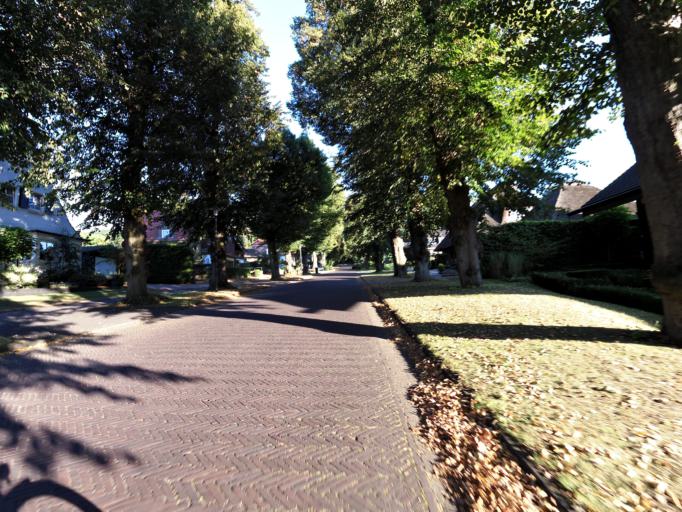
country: DE
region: North Rhine-Westphalia
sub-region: Regierungsbezirk Dusseldorf
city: Kleve
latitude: 51.8686
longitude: 6.1639
